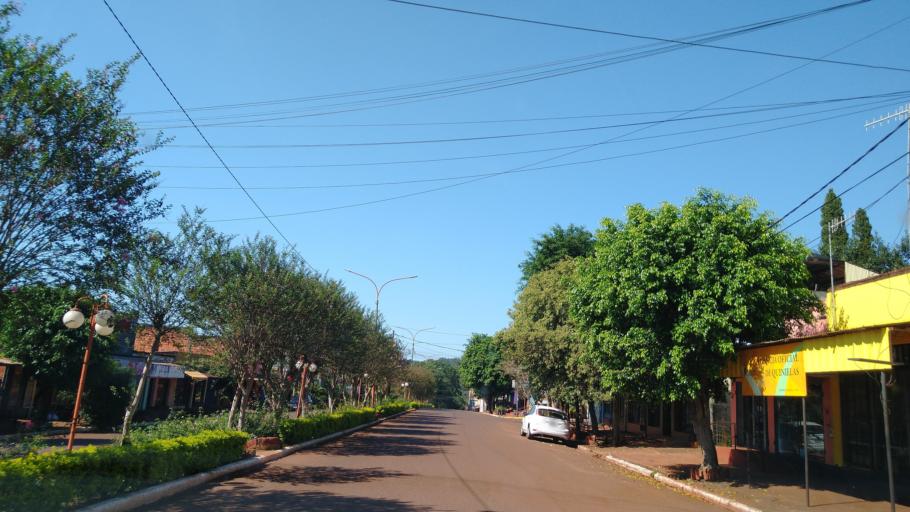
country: AR
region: Misiones
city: Puerto Esperanza
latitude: -26.0238
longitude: -54.6125
